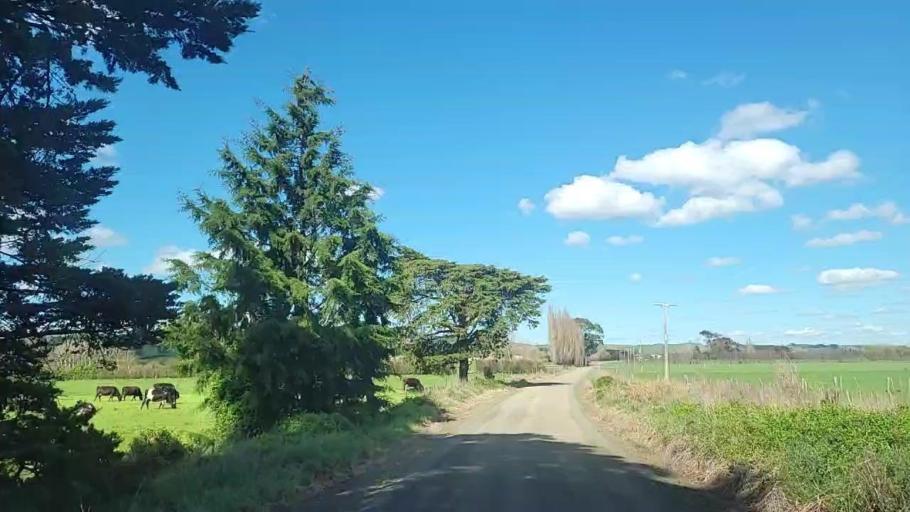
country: NZ
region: Waikato
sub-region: Hauraki District
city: Ngatea
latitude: -37.5063
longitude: 175.4412
